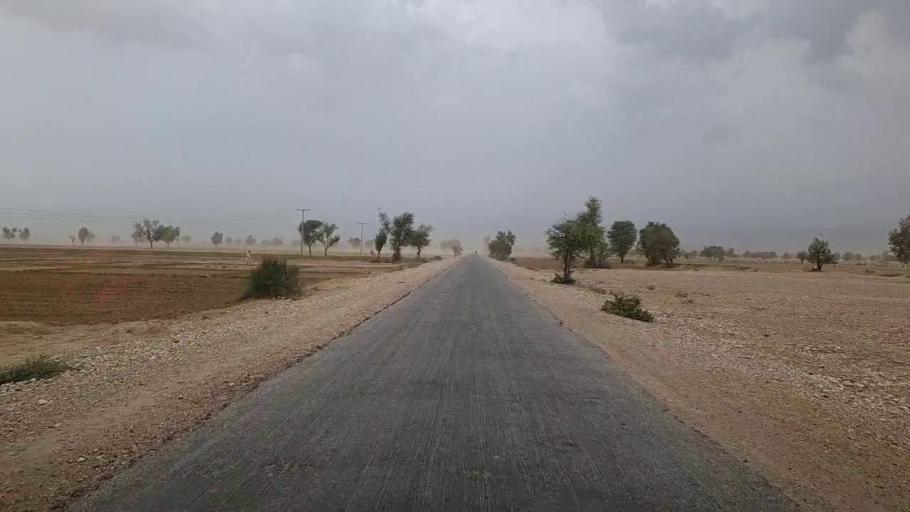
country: PK
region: Sindh
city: Sehwan
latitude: 26.3178
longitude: 67.7305
